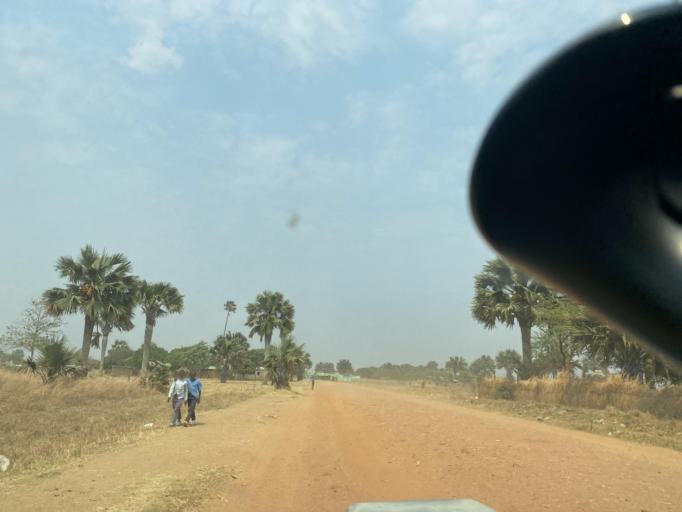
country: ZM
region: Lusaka
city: Kafue
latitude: -15.6622
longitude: 28.0226
